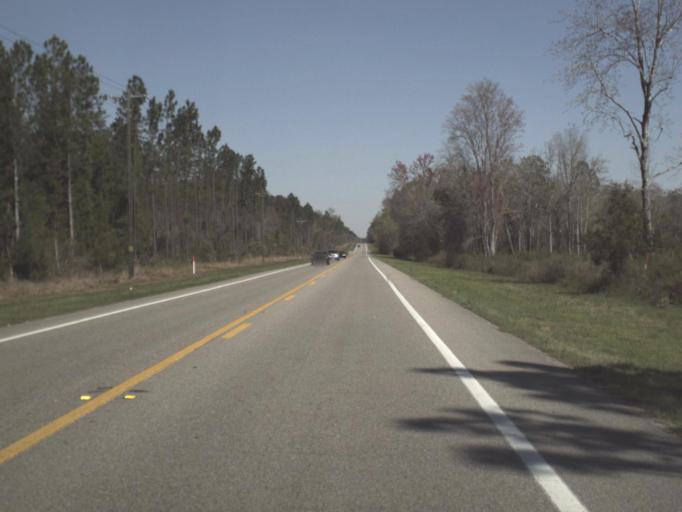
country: US
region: Florida
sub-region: Gadsden County
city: Gretna
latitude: 30.3848
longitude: -84.7204
